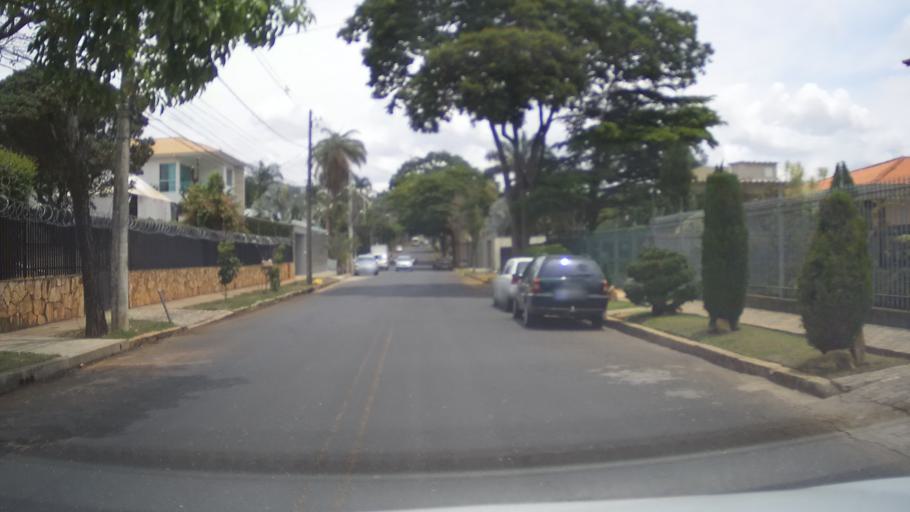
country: BR
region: Minas Gerais
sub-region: Belo Horizonte
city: Belo Horizonte
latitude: -19.8566
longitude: -43.9681
